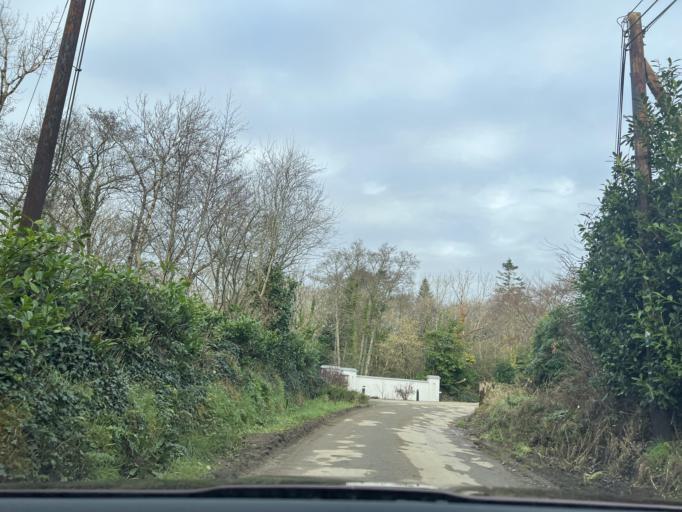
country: IE
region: Leinster
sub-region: Loch Garman
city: Loch Garman
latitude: 52.3683
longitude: -6.5345
